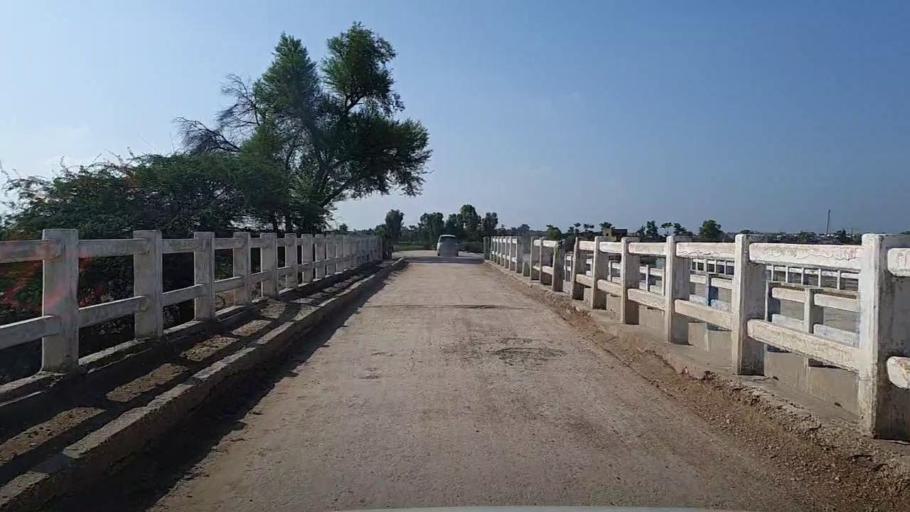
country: PK
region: Sindh
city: Kandiaro
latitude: 27.0733
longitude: 68.3130
